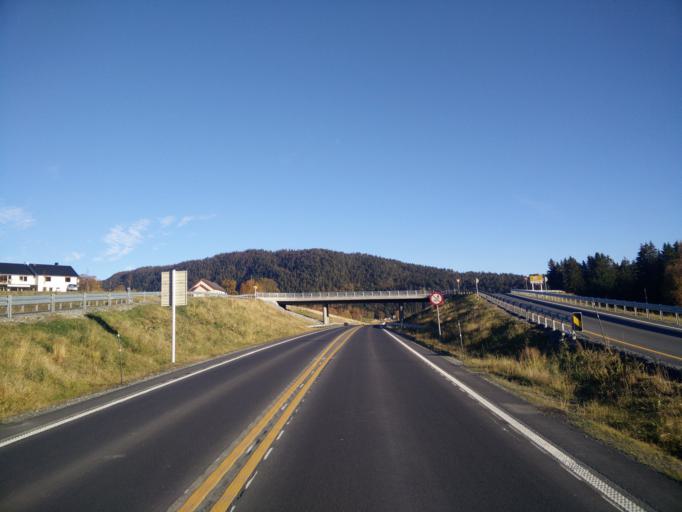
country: NO
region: Sor-Trondelag
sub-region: Snillfjord
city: Krokstadora
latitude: 63.2865
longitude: 9.6278
